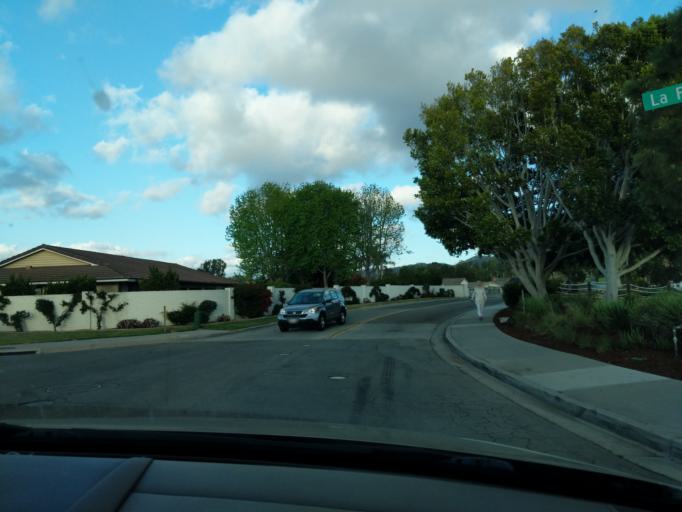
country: US
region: California
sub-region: San Diego County
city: Lake San Marcos
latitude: 33.1252
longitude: -117.2065
